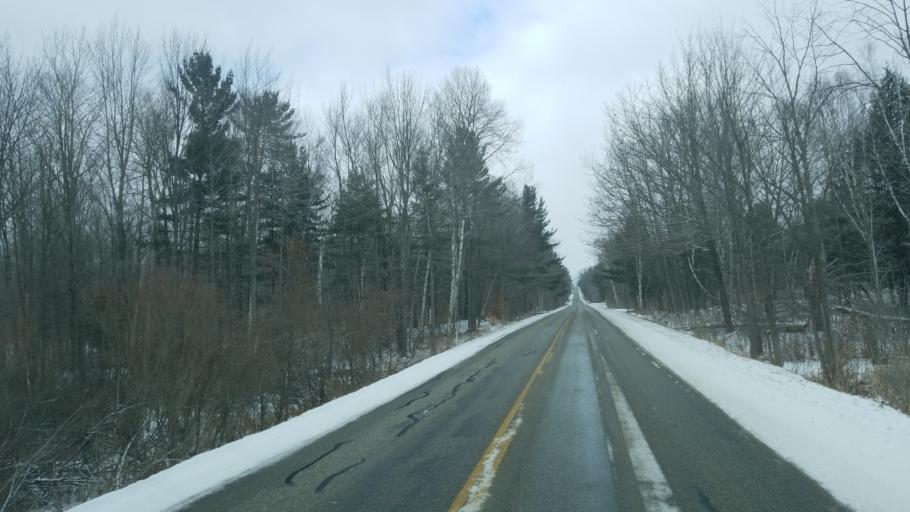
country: US
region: Michigan
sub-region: Osceola County
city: Evart
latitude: 43.9557
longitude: -85.2468
